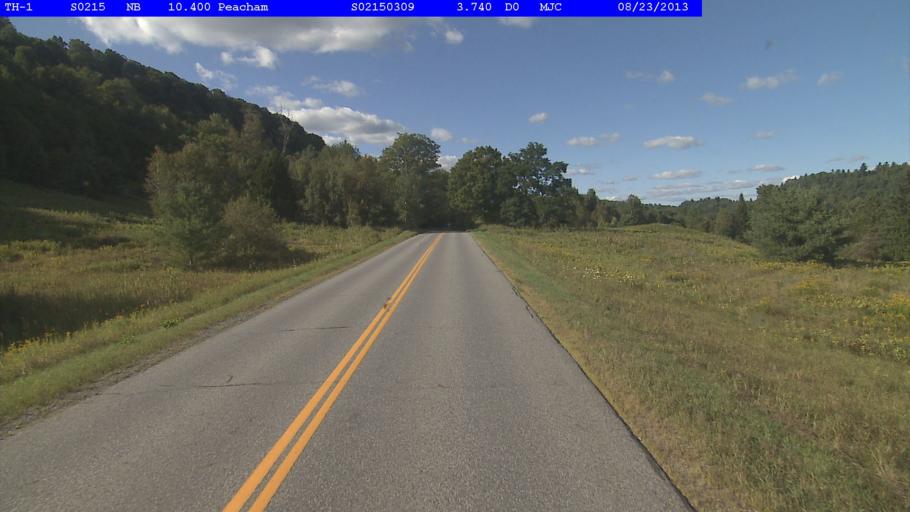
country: US
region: Vermont
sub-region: Caledonia County
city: Saint Johnsbury
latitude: 44.3502
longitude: -72.1777
